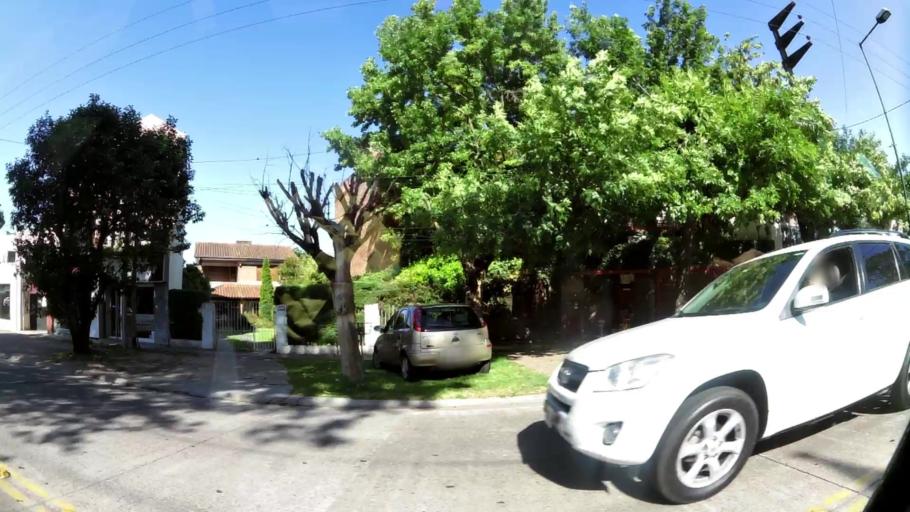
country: AR
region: Buenos Aires
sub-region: Partido de San Isidro
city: San Isidro
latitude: -34.4832
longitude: -58.5557
